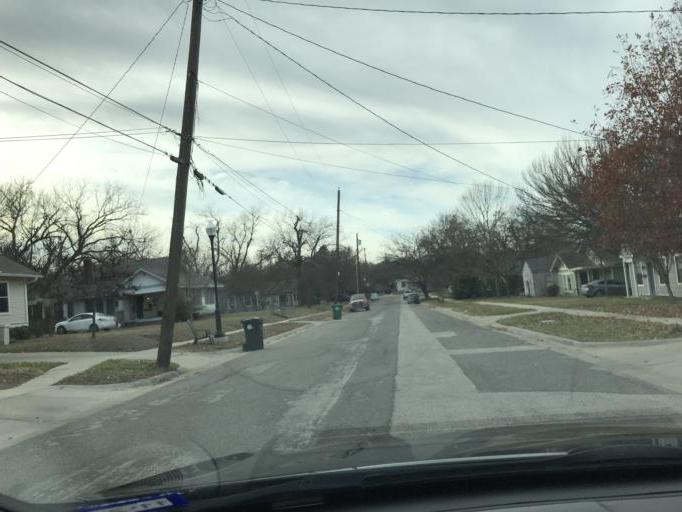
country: US
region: Texas
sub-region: Denton County
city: Denton
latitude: 33.2179
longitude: -97.1407
